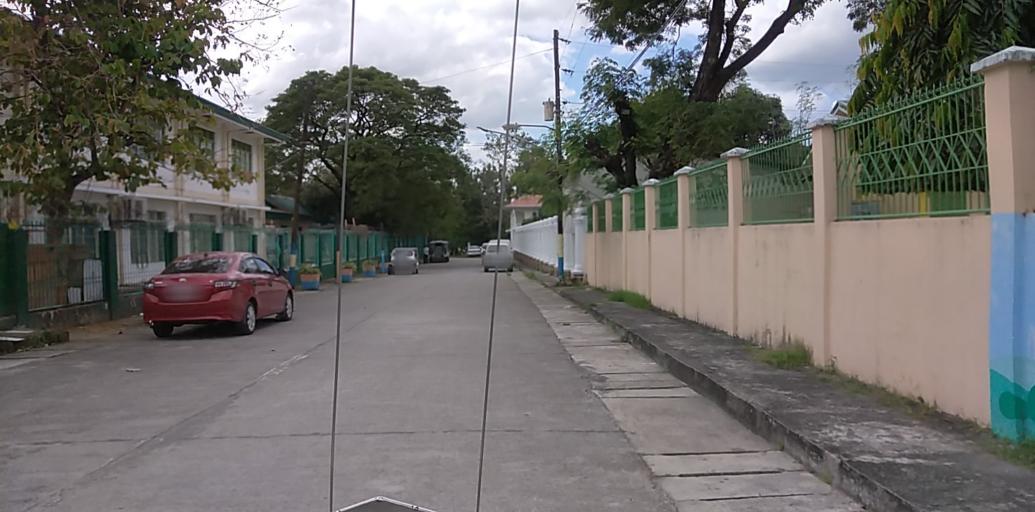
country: PH
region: Central Luzon
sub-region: Province of Pampanga
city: Porac
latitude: 15.0720
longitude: 120.5393
